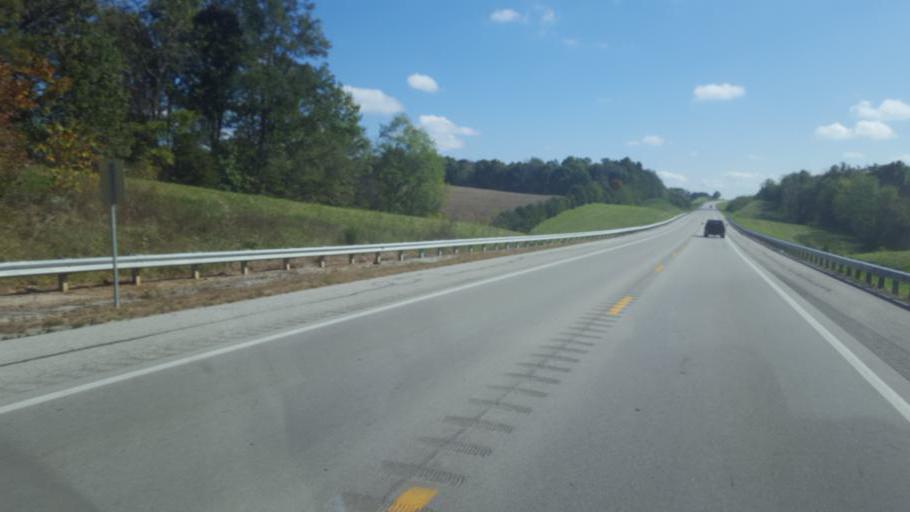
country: US
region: Kentucky
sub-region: Mason County
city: Maysville
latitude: 38.5811
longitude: -83.6726
